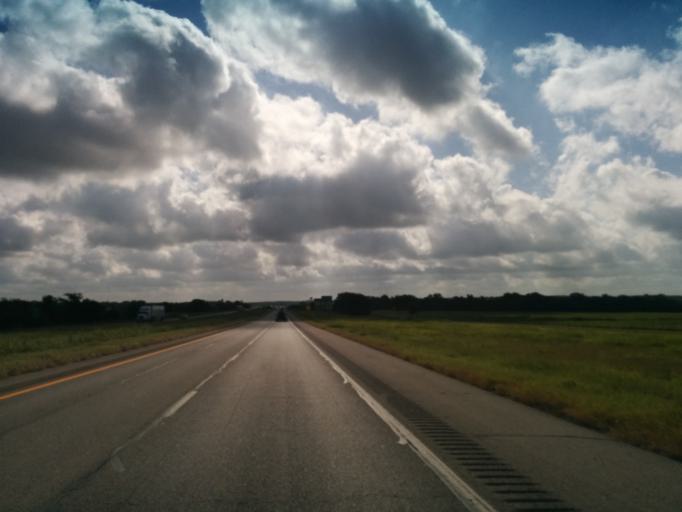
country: US
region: Texas
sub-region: Caldwell County
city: Luling
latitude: 29.6496
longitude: -97.6095
